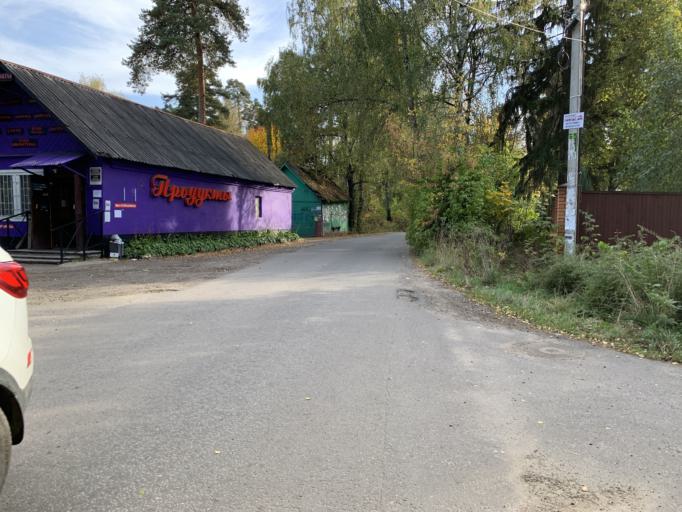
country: RU
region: Moskovskaya
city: Mamontovka
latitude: 55.9859
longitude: 37.8313
